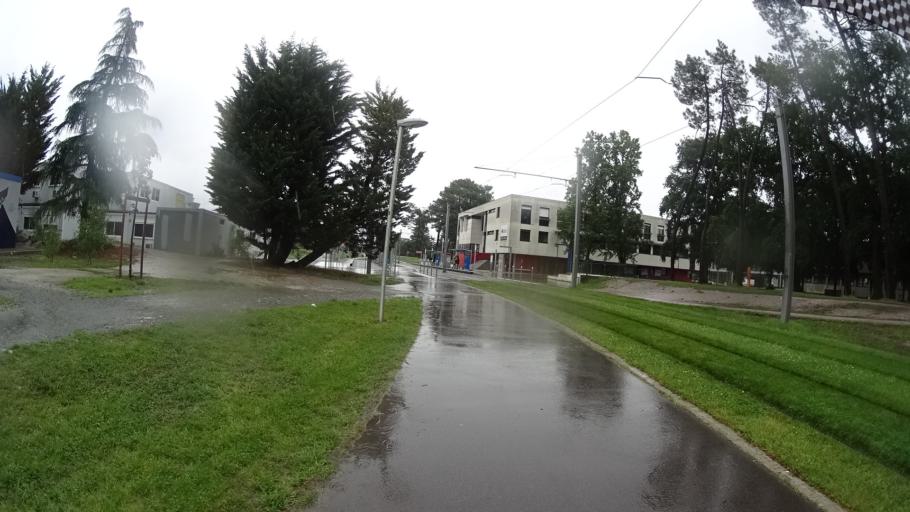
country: FR
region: Aquitaine
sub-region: Departement de la Gironde
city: Talence
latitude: 44.7967
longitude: -0.6183
